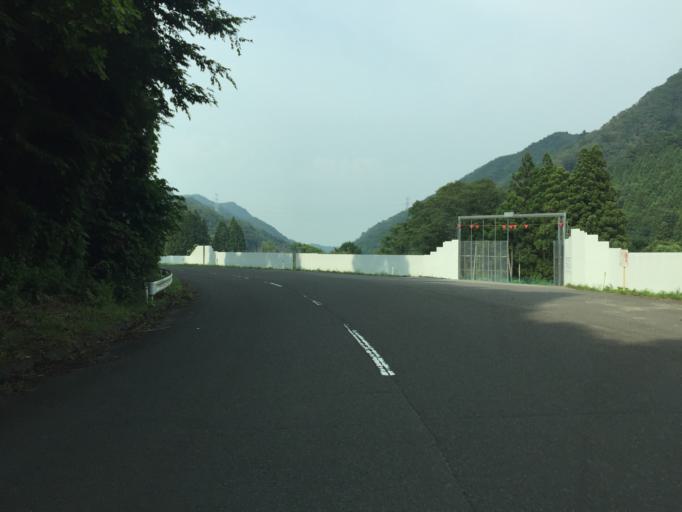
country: JP
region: Fukushima
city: Namie
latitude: 37.5670
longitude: 140.8766
